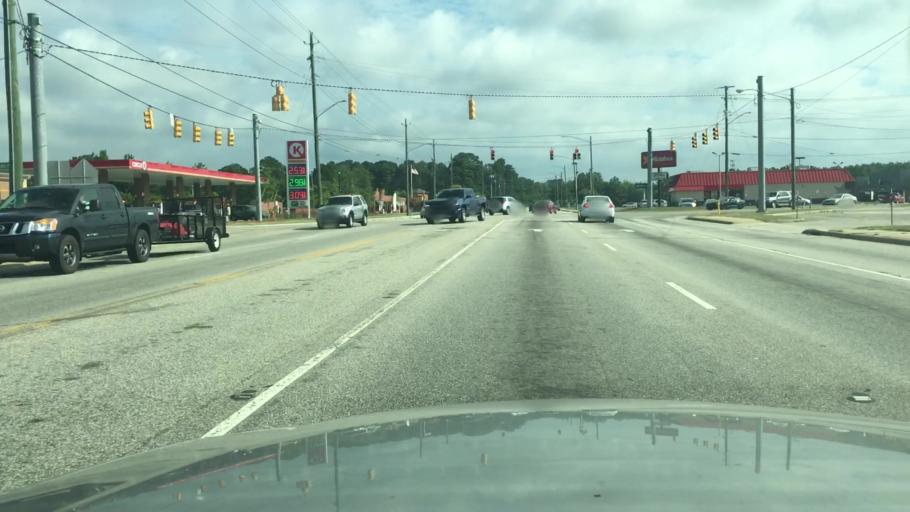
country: US
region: North Carolina
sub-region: Cumberland County
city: Hope Mills
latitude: 35.0045
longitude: -78.9671
